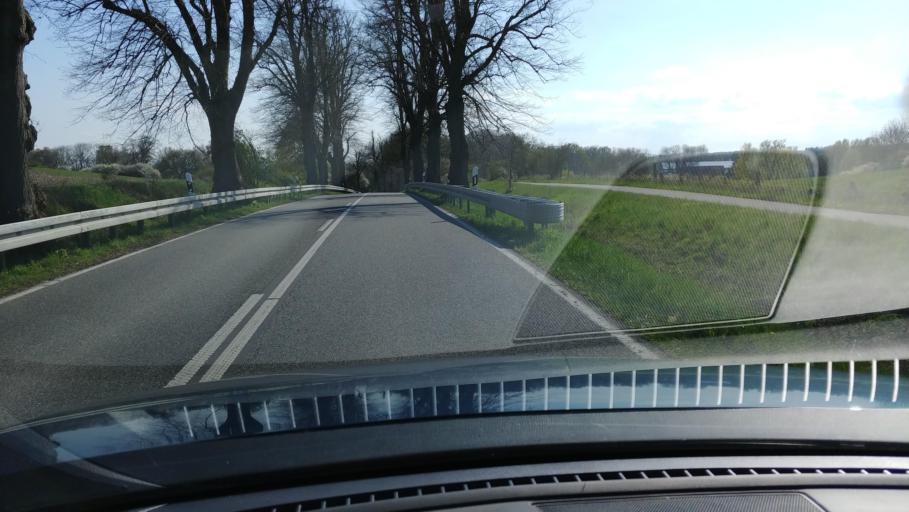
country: DE
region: Mecklenburg-Vorpommern
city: Muhlen Eichsen
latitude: 53.7654
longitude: 11.2616
